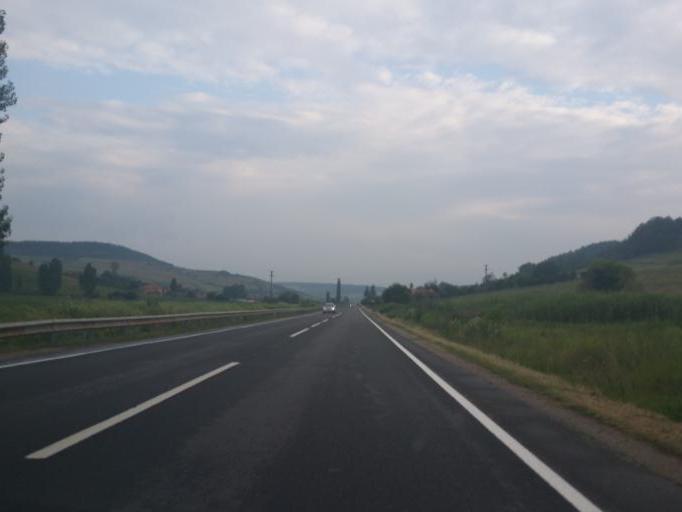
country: RO
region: Cluj
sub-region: Comuna Sanpaul
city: Sanpaul
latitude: 46.8807
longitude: 23.4203
